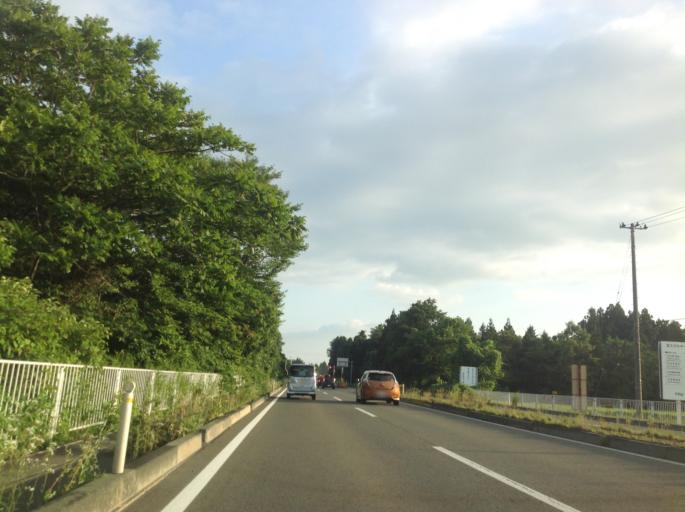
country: JP
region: Iwate
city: Hanamaki
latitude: 39.4813
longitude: 141.1404
